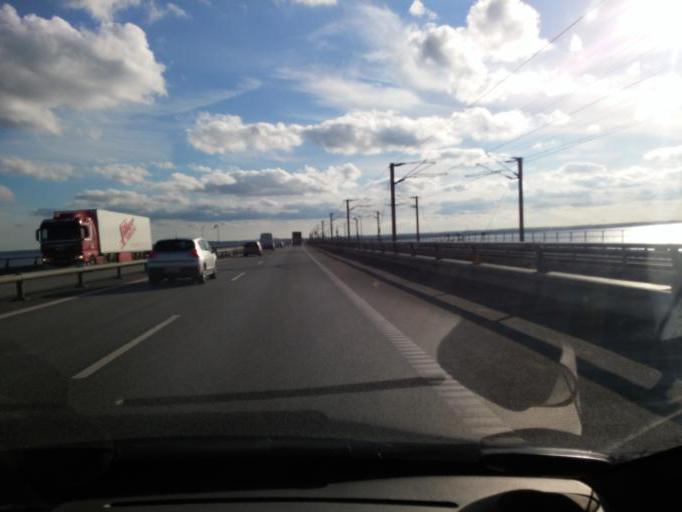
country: DK
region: South Denmark
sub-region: Nyborg Kommune
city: Nyborg
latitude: 55.3065
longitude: 10.8862
